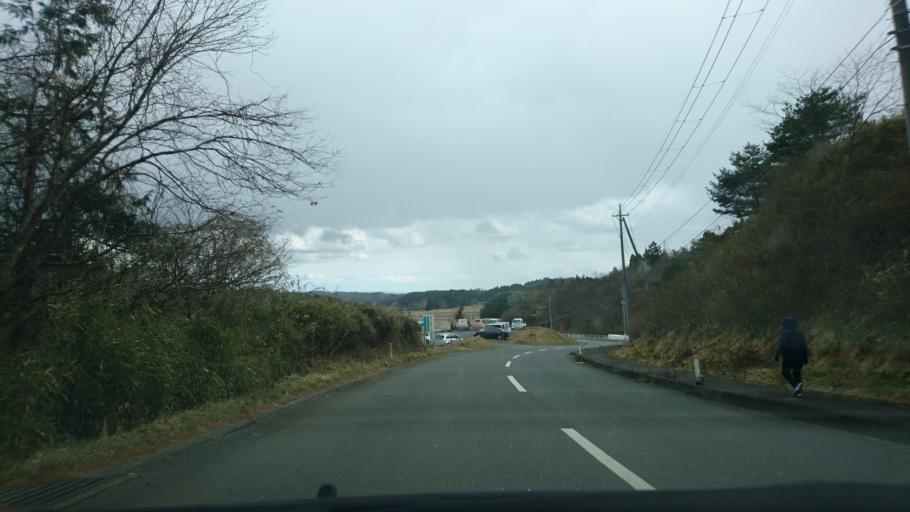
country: JP
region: Iwate
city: Ichinoseki
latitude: 38.8293
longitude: 141.1732
